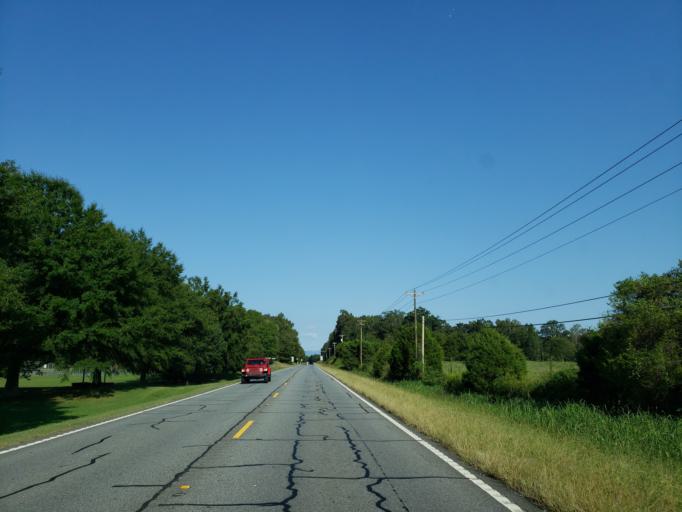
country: US
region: Georgia
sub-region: Whitfield County
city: Varnell
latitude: 34.8947
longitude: -84.9417
